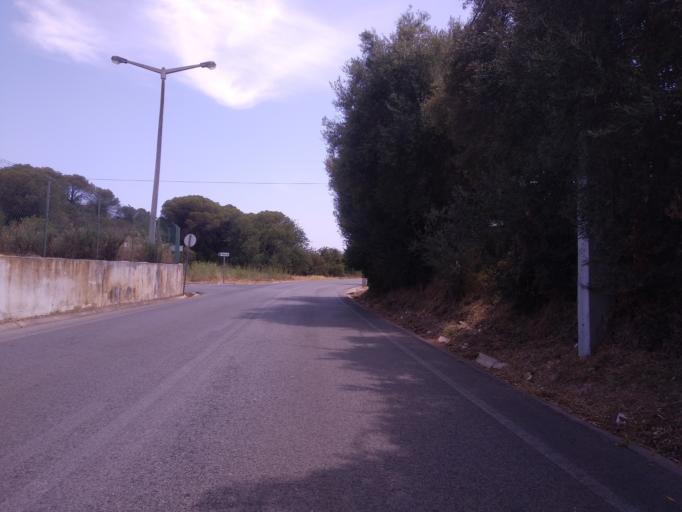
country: PT
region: Faro
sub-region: Loule
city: Almancil
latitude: 37.0792
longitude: -8.0011
